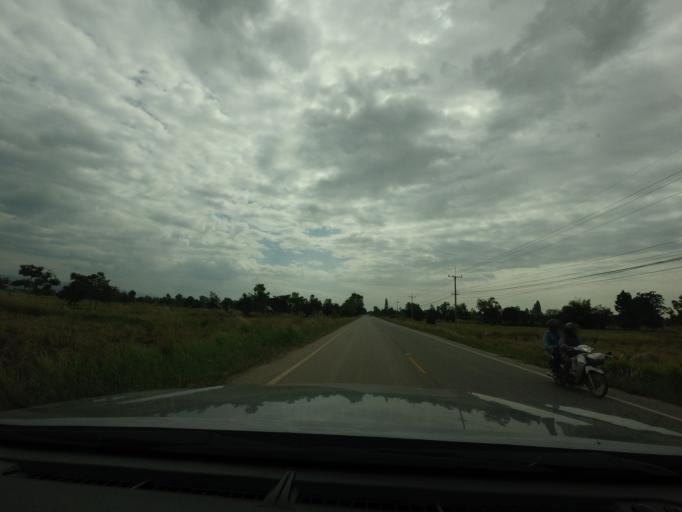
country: TH
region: Phitsanulok
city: Noen Maprang
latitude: 16.6343
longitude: 100.6178
